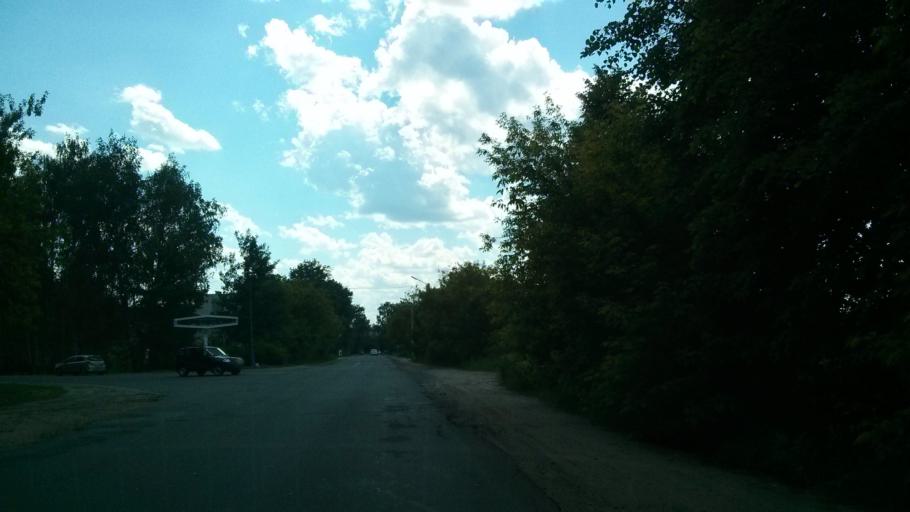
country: RU
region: Vladimir
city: Murom
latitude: 55.5377
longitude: 41.9779
